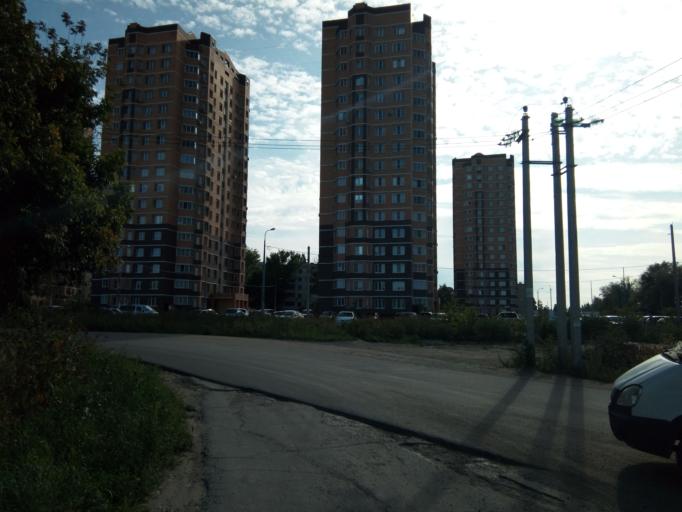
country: RU
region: Lipetsk
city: Lipetsk
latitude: 52.6356
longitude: 39.5462
